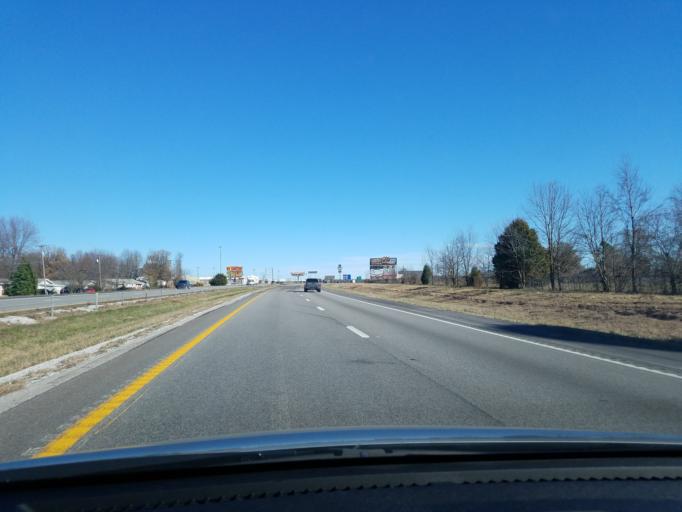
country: US
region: Missouri
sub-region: Greene County
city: Strafford
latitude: 37.2711
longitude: -93.1258
